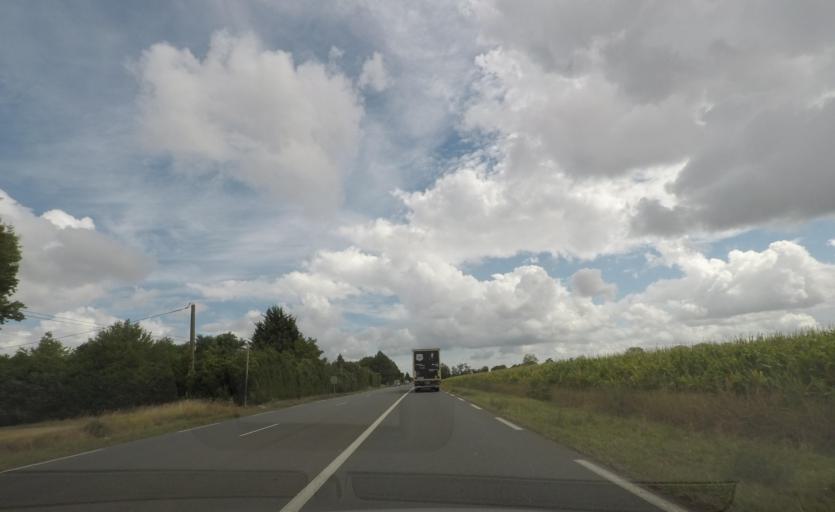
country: FR
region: Pays de la Loire
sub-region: Departement de Maine-et-Loire
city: Seiches-sur-le-Loir
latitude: 47.5617
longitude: -0.3712
